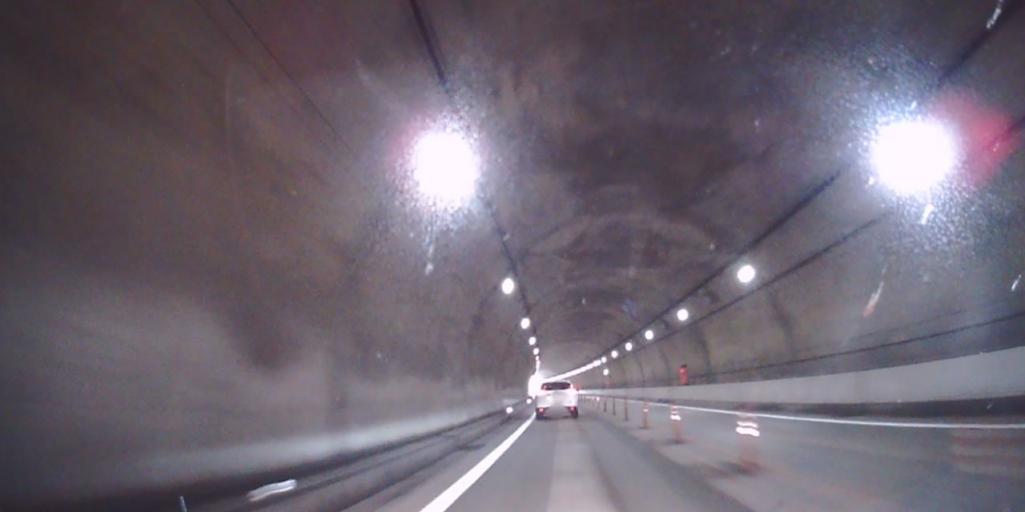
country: JP
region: Hokkaido
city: Niseko Town
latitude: 42.5925
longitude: 140.7122
